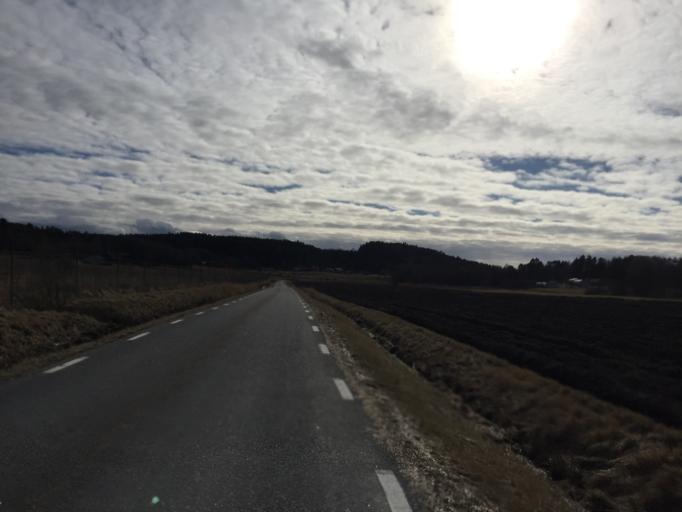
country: SE
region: Vaestra Goetaland
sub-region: Kungalvs Kommun
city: Diserod
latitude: 57.9303
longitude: 11.9674
